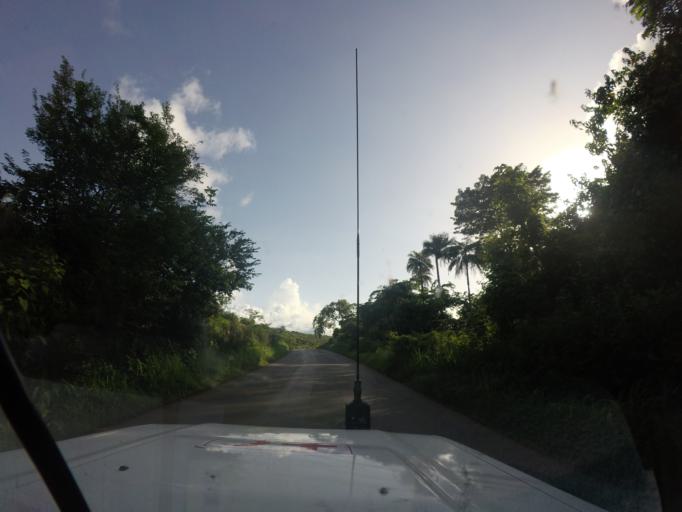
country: GN
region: Kindia
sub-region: Kindia
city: Kindia
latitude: 10.0181
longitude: -12.8131
